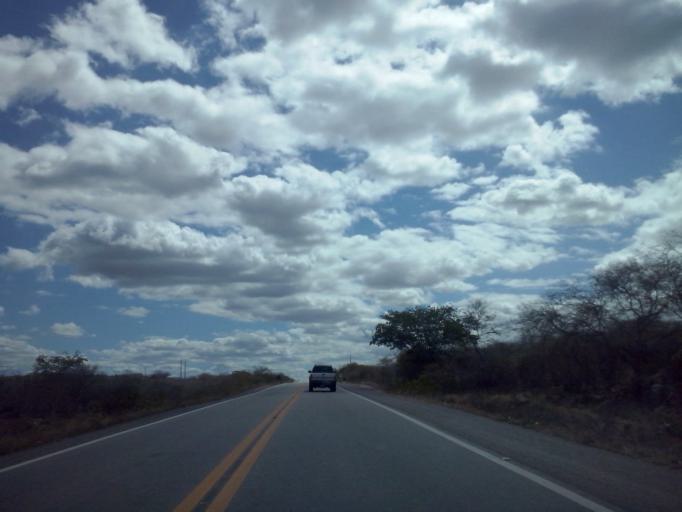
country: BR
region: Paraiba
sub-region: Soledade
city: Soledade
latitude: -7.0414
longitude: -36.4046
